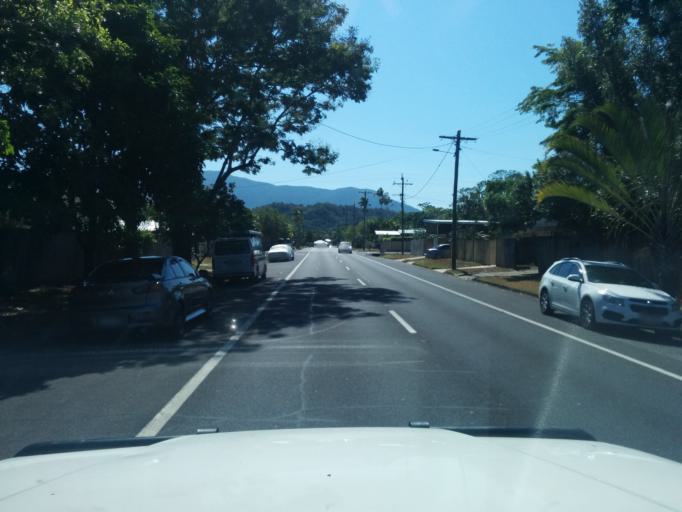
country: AU
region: Queensland
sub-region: Cairns
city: Cairns
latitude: -16.9027
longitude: 145.7372
